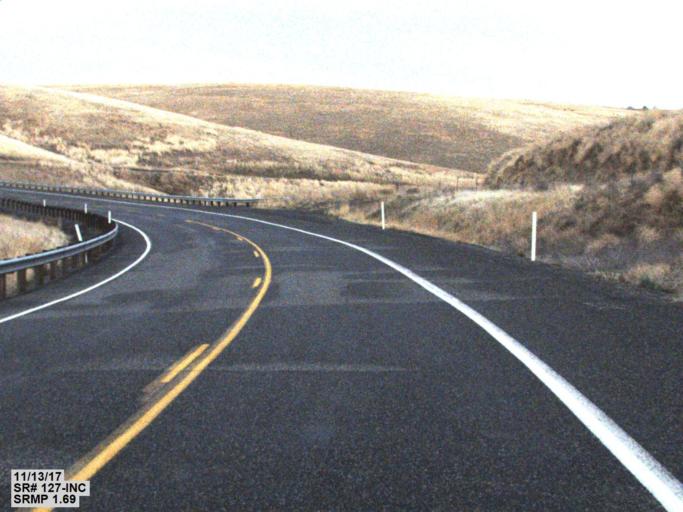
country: US
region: Washington
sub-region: Garfield County
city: Pomeroy
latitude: 46.5255
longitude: -117.7886
